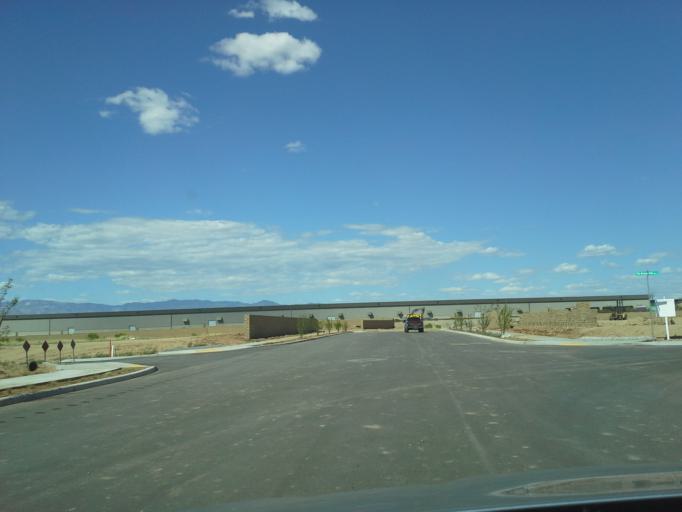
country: US
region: Arizona
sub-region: Pima County
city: Summit
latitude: 32.1212
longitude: -110.8493
